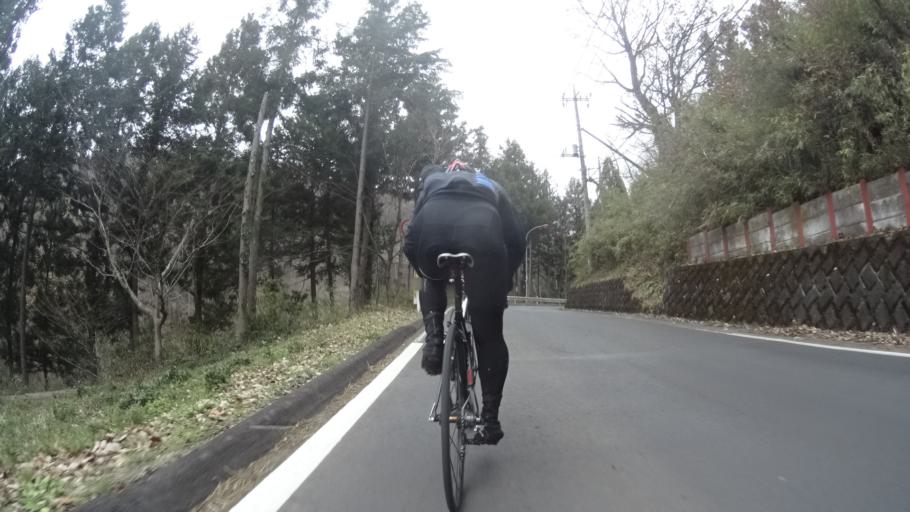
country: JP
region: Yamanashi
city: Uenohara
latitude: 35.6365
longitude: 139.1259
